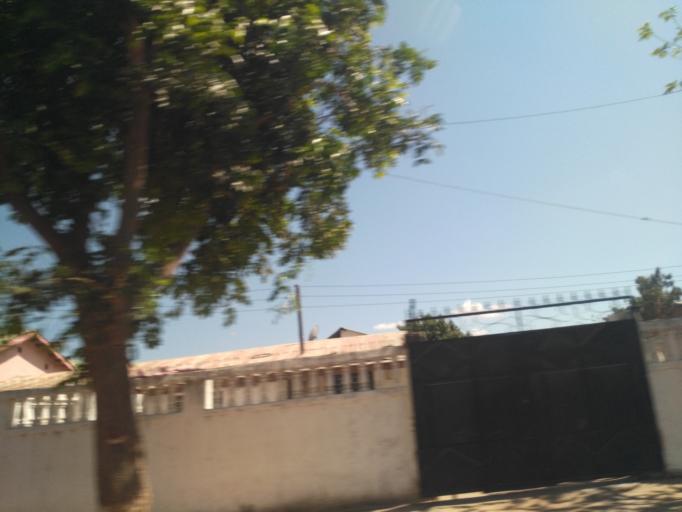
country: TZ
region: Dodoma
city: Dodoma
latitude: -6.1656
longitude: 35.7481
